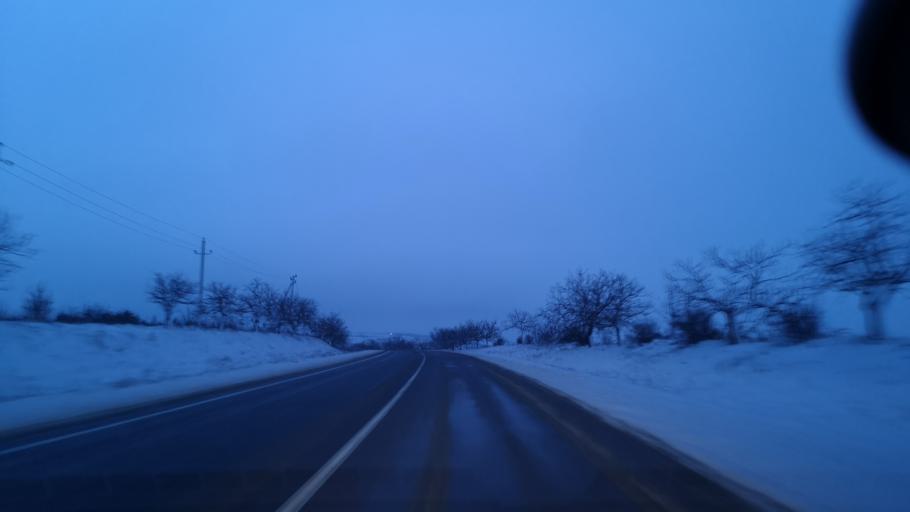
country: MD
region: Soldanesti
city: Soldanesti
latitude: 47.7191
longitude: 28.8487
